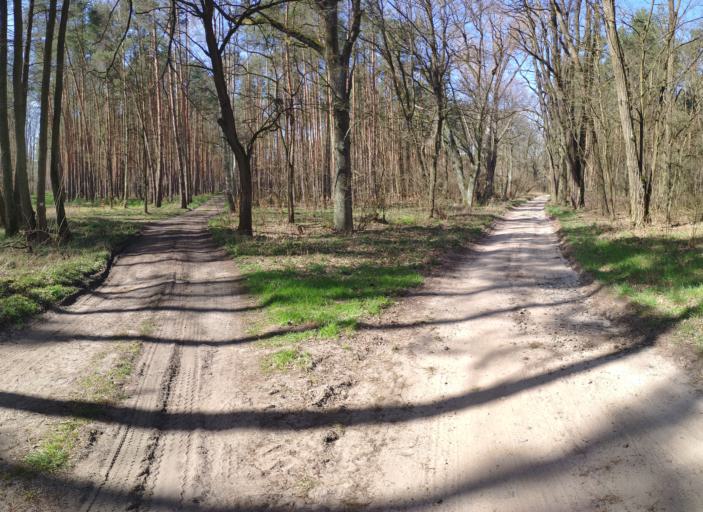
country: PL
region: Lubusz
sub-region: Powiat krosnienski
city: Dabie
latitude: 52.0368
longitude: 15.2361
